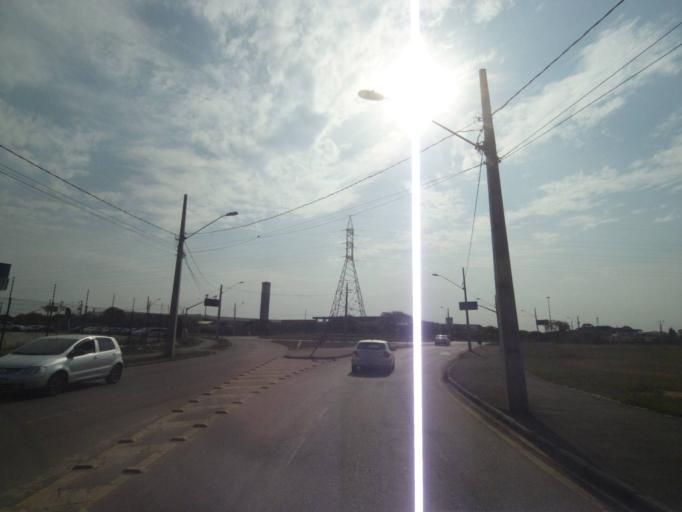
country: BR
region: Parana
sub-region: Sao Jose Dos Pinhais
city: Sao Jose dos Pinhais
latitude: -25.5026
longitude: -49.2102
